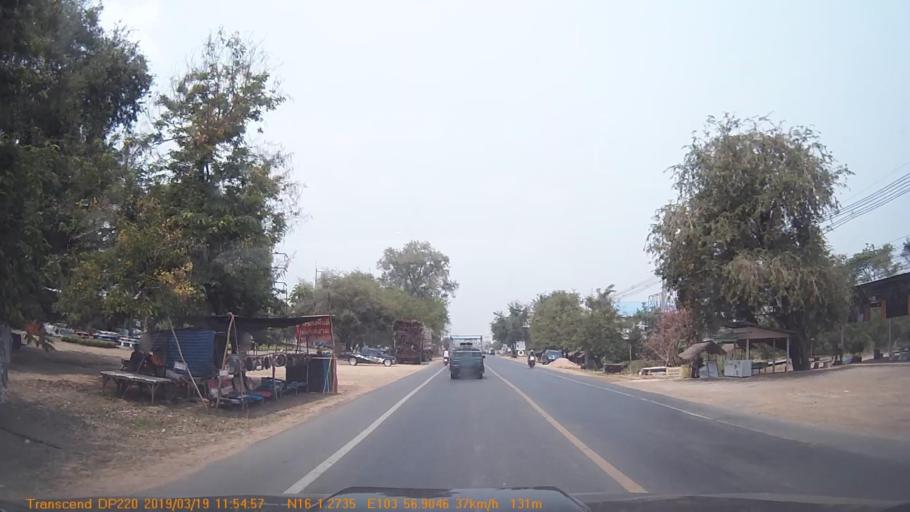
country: TH
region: Roi Et
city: Ban Selaphum
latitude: 16.0213
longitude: 103.9483
